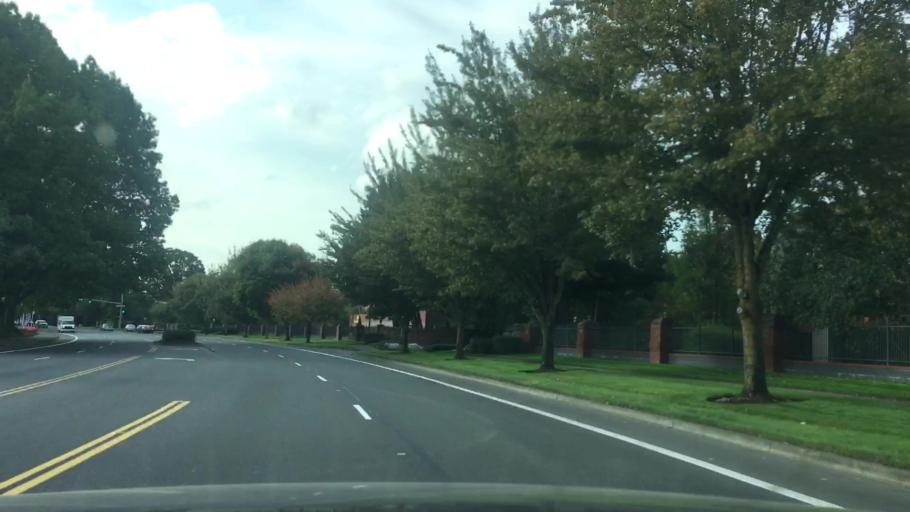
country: US
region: Oregon
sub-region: Lane County
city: Eugene
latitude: 44.0864
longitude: -123.1046
